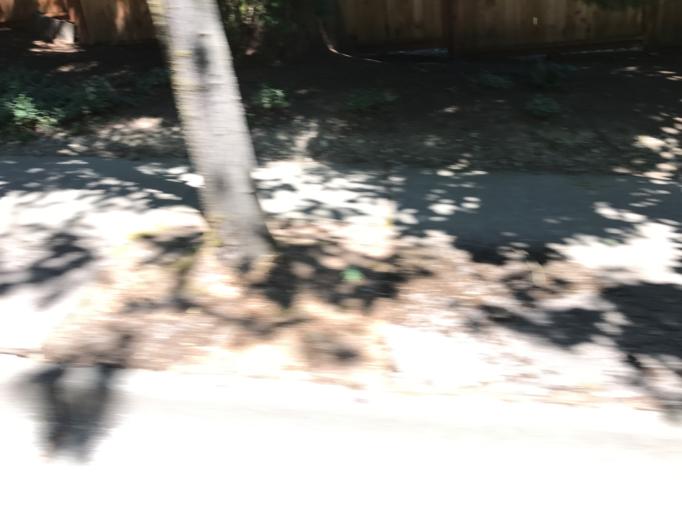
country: US
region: Washington
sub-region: King County
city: Redmond
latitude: 47.6461
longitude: -122.1188
